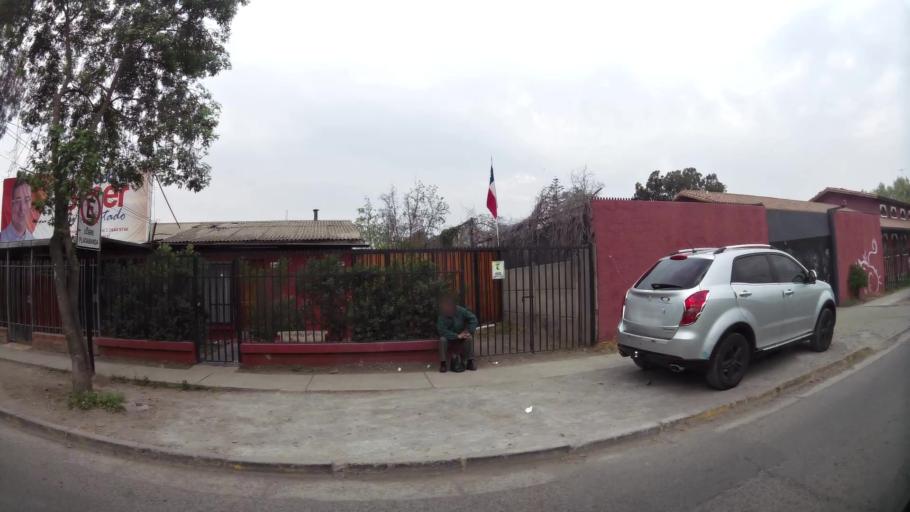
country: CL
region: Santiago Metropolitan
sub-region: Provincia de Chacabuco
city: Chicureo Abajo
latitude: -33.2012
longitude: -70.6752
